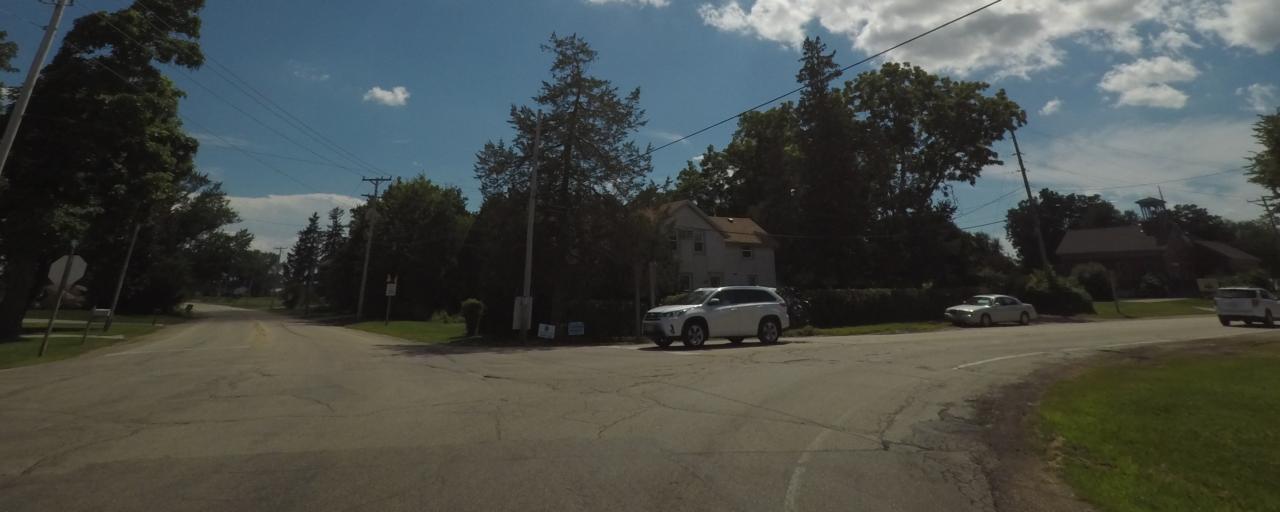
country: US
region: Wisconsin
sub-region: Dane County
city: Fitchburg
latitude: 42.9295
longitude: -89.5221
